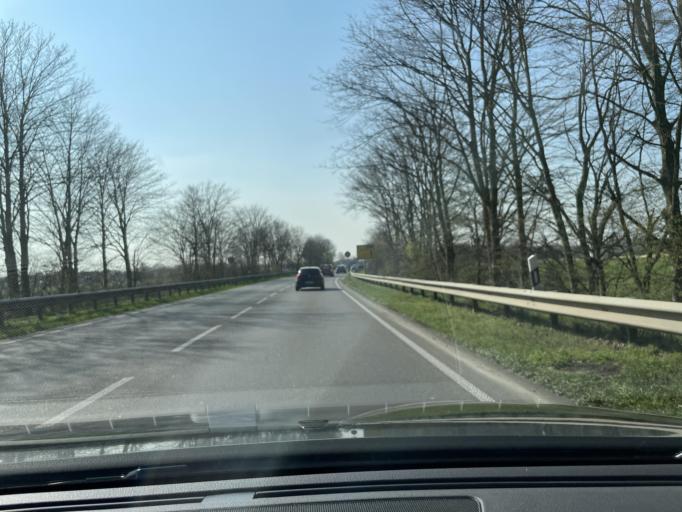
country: DE
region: North Rhine-Westphalia
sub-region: Regierungsbezirk Dusseldorf
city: Korschenbroich
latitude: 51.2192
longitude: 6.5136
